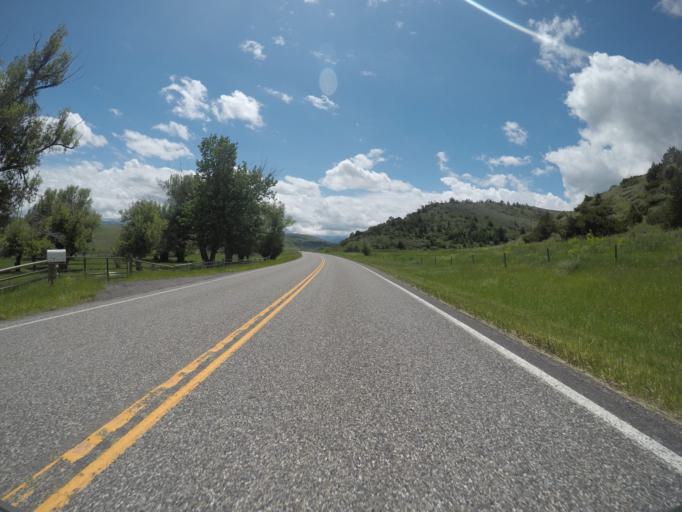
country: US
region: Montana
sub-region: Sweet Grass County
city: Big Timber
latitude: 45.6784
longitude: -110.0880
